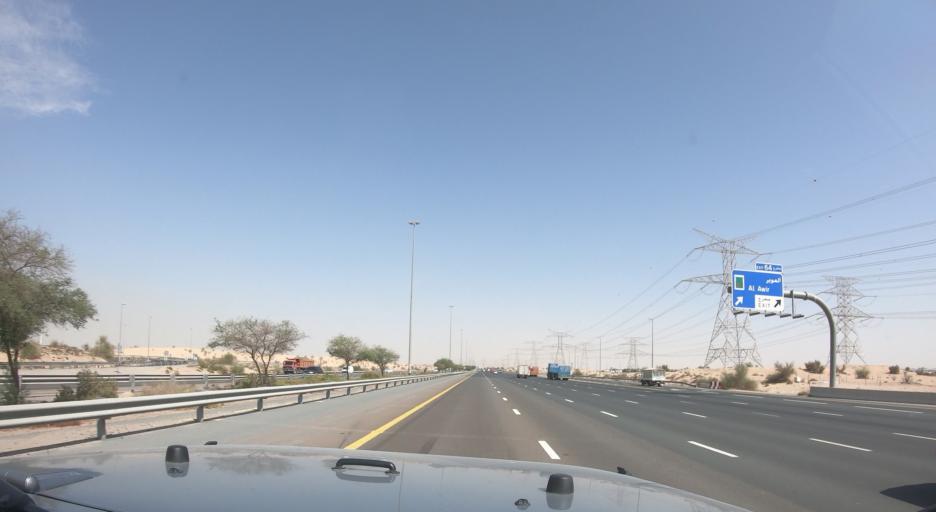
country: AE
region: Ash Shariqah
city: Sharjah
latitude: 25.1893
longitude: 55.5298
